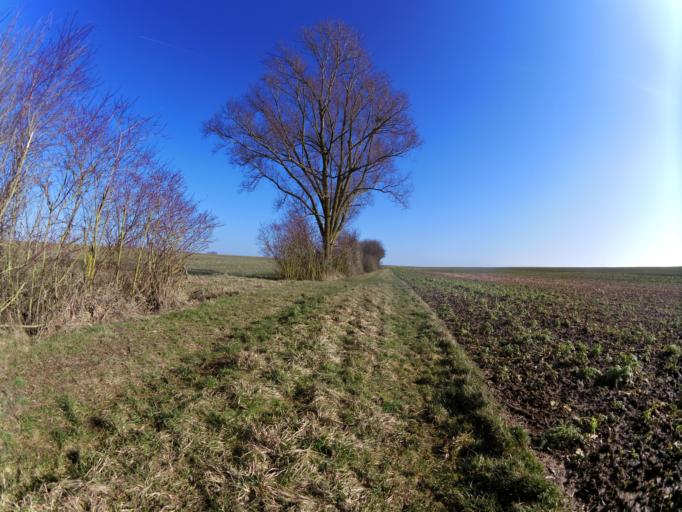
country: DE
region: Bavaria
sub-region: Regierungsbezirk Unterfranken
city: Giebelstadt
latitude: 49.6885
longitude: 9.9676
